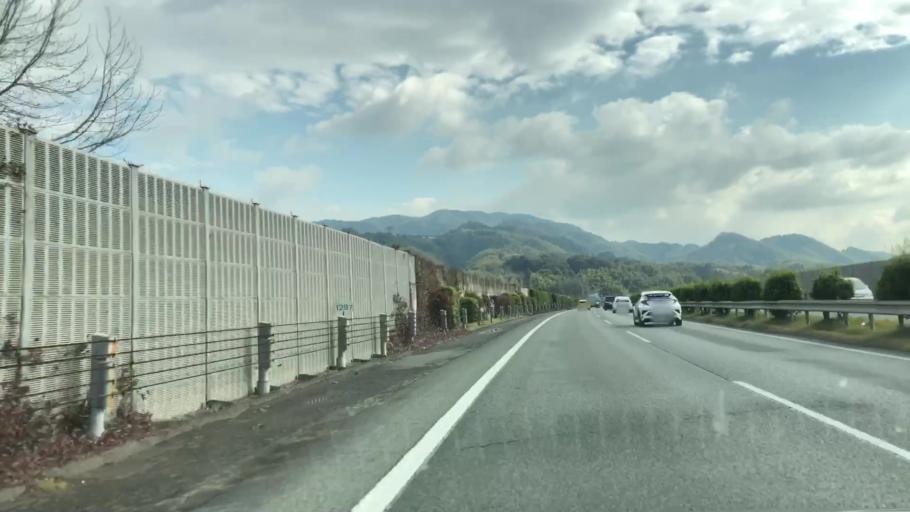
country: JP
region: Fukuoka
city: Setakamachi-takayanagi
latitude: 33.1166
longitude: 130.5270
